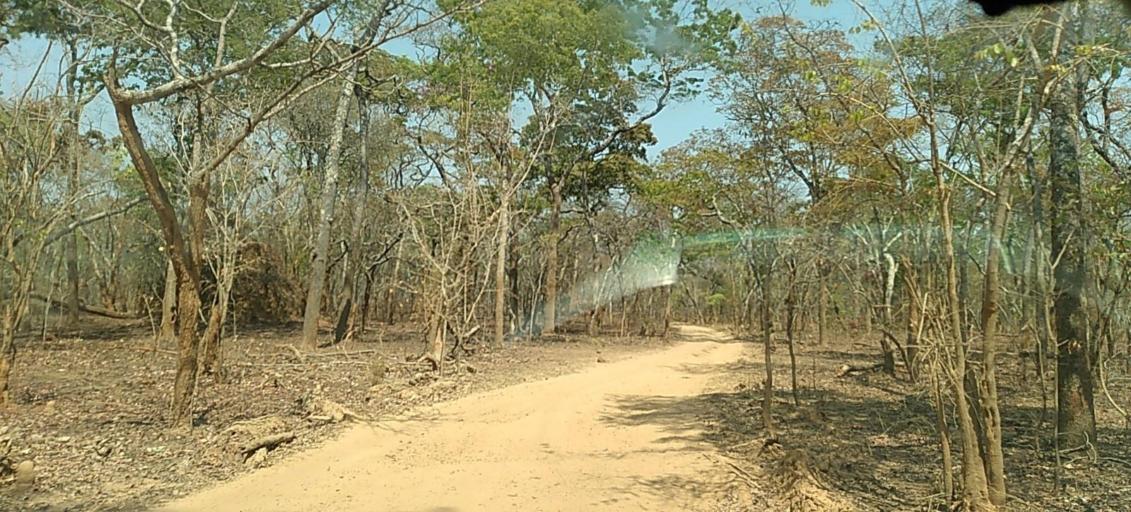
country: ZM
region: North-Western
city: Kasempa
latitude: -13.3928
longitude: 25.6144
